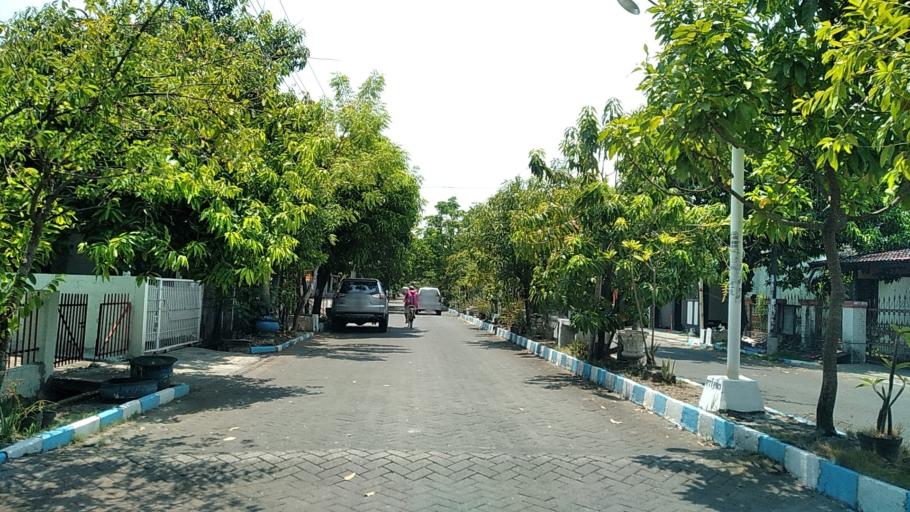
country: ID
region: Central Java
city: Mranggen
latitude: -7.0062
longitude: 110.4811
